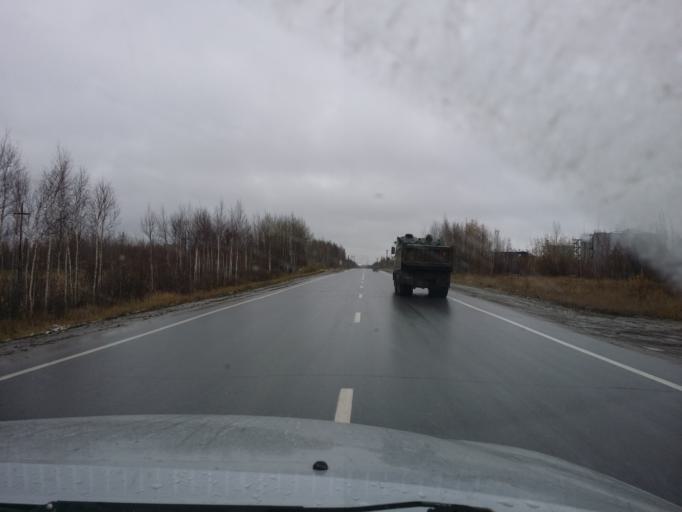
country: RU
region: Khanty-Mansiyskiy Avtonomnyy Okrug
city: Megion
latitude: 61.0694
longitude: 76.1159
